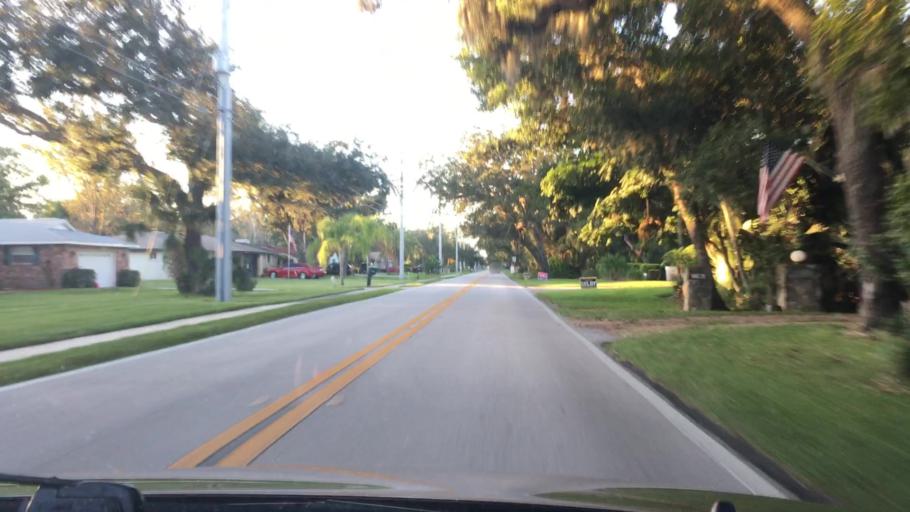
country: US
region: Florida
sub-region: Volusia County
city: Ormond Beach
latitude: 29.3057
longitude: -81.0655
